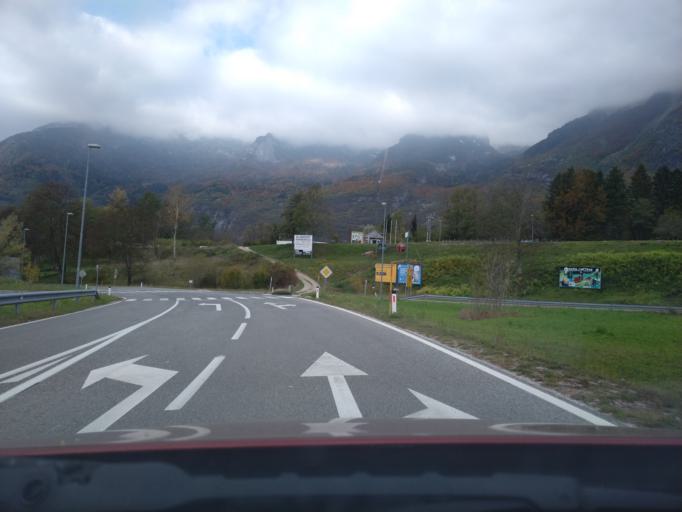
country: SI
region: Bovec
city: Bovec
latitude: 46.3323
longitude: 13.5407
